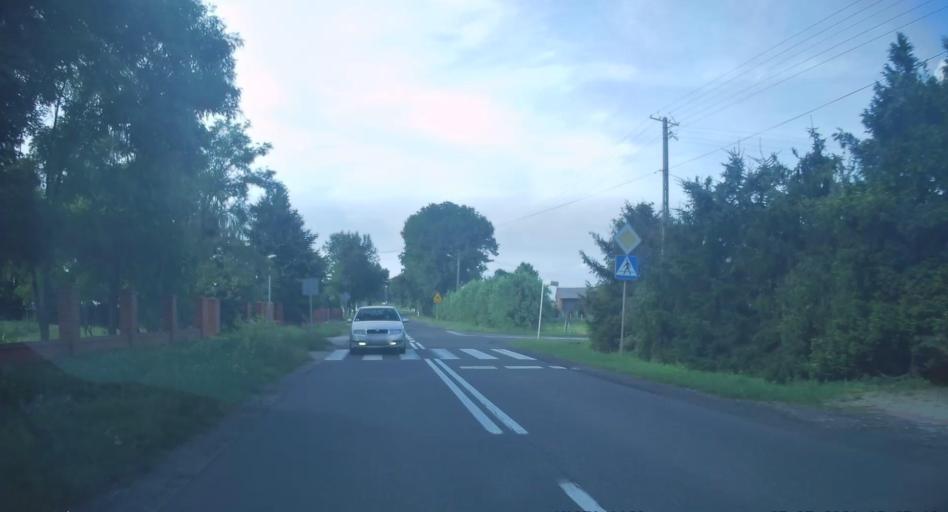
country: PL
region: Lodz Voivodeship
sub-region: Powiat tomaszowski
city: Rzeczyca
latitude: 51.6060
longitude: 20.2935
